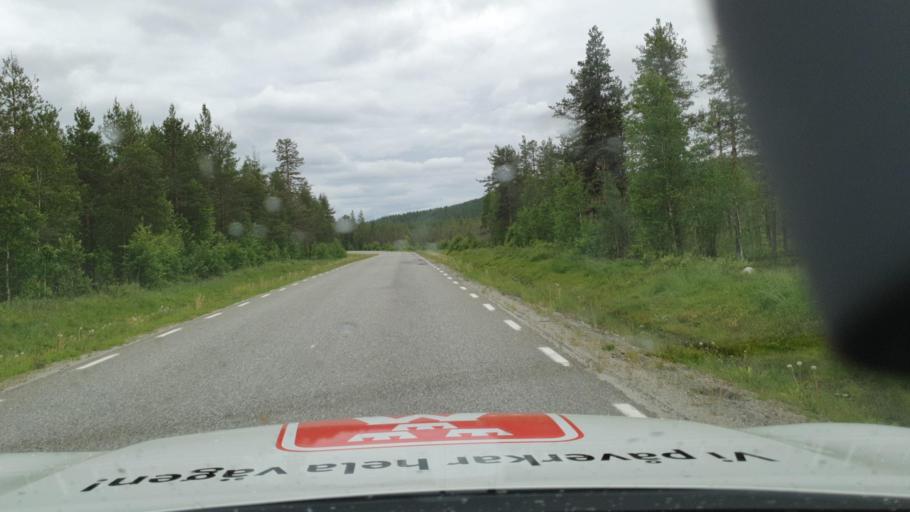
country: SE
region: Vaesterbotten
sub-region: Lycksele Kommun
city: Soderfors
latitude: 64.2689
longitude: 18.2034
